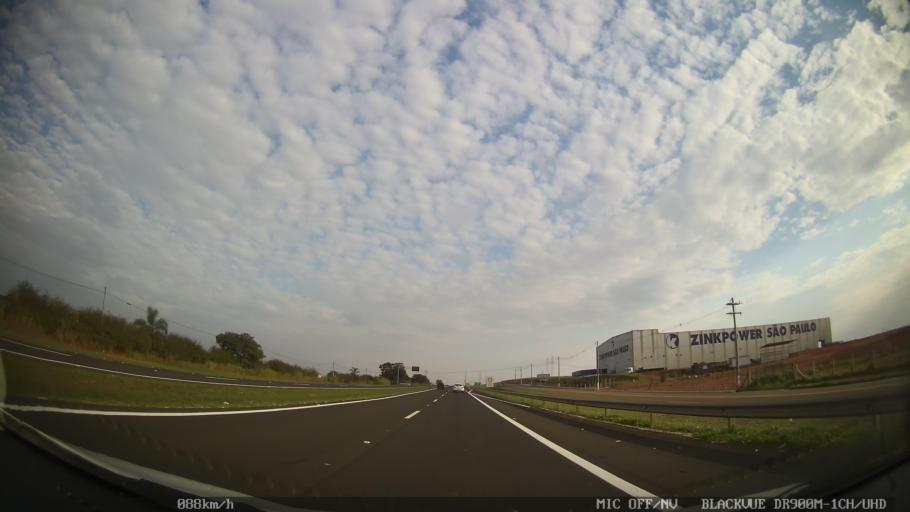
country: BR
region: Sao Paulo
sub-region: Artur Nogueira
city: Artur Nogueira
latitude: -22.5984
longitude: -47.1885
